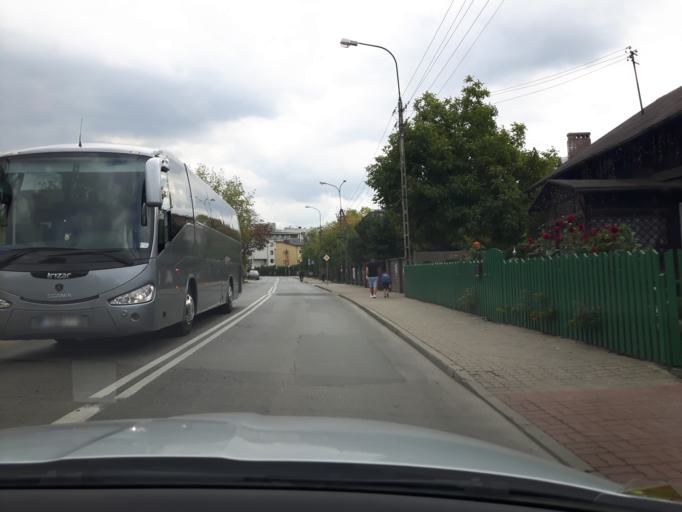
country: PL
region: Masovian Voivodeship
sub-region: Warszawa
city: Rembertow
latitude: 52.2613
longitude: 21.1592
